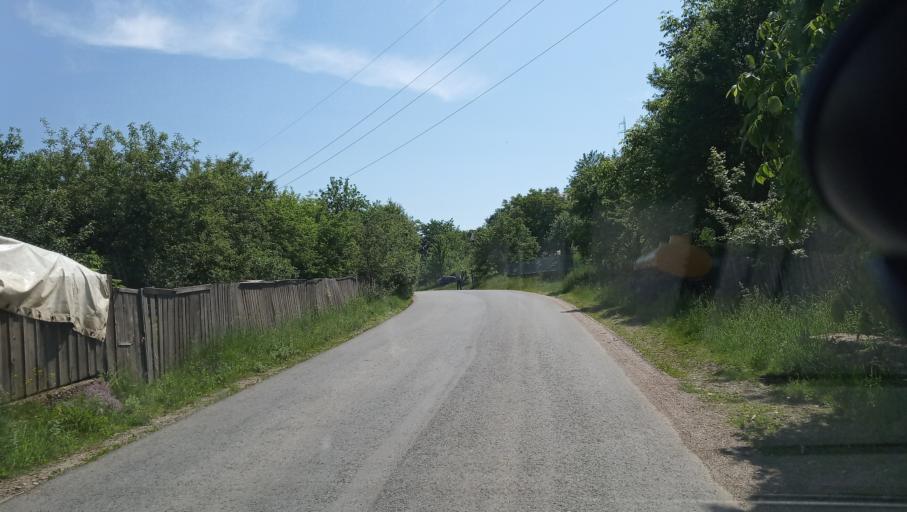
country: RO
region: Cluj
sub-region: Comuna Gilau
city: Gilau
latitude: 46.7303
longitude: 23.3220
